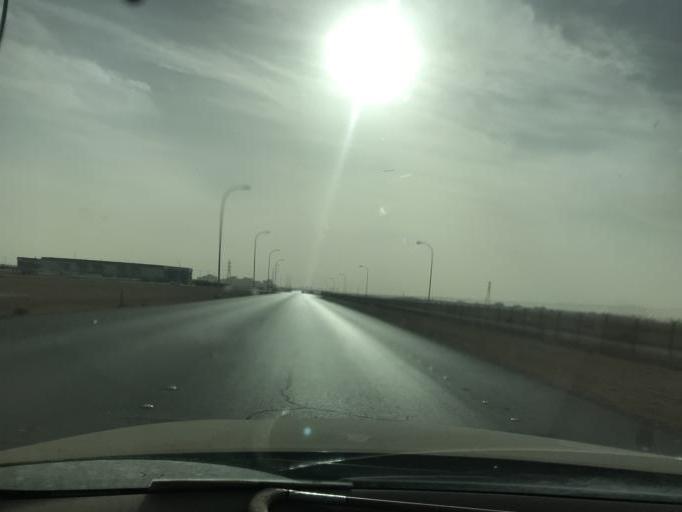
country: SA
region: Ar Riyad
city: Riyadh
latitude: 24.9214
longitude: 46.7012
